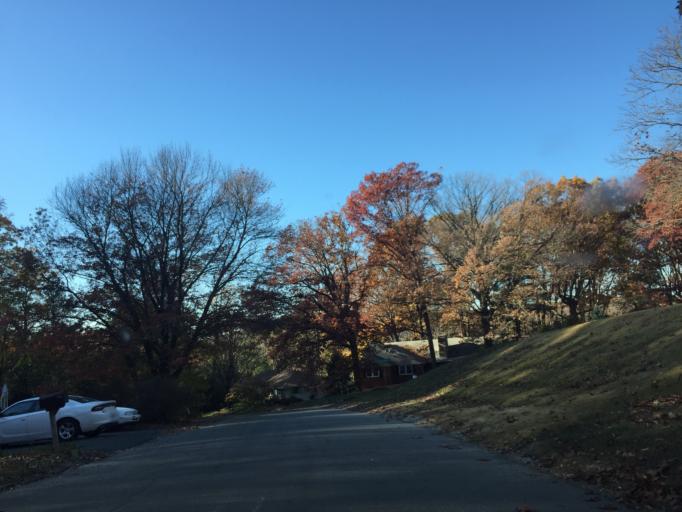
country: US
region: Maryland
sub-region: Baltimore County
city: Parkville
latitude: 39.4054
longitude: -76.5544
